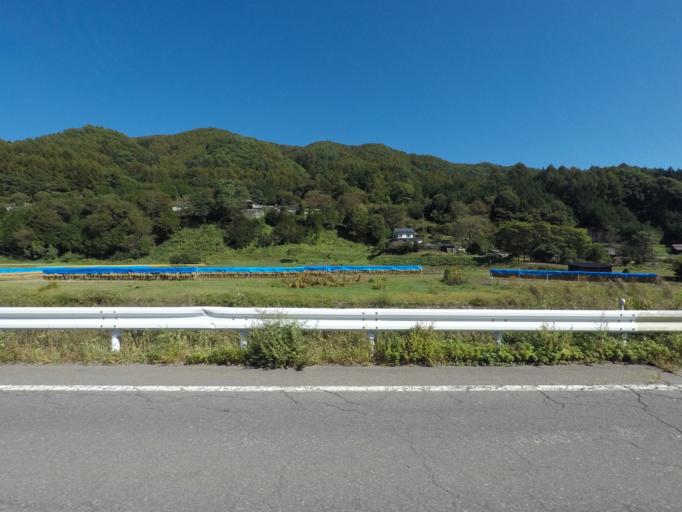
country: JP
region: Nagano
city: Tatsuno
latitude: 35.9723
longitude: 137.7545
